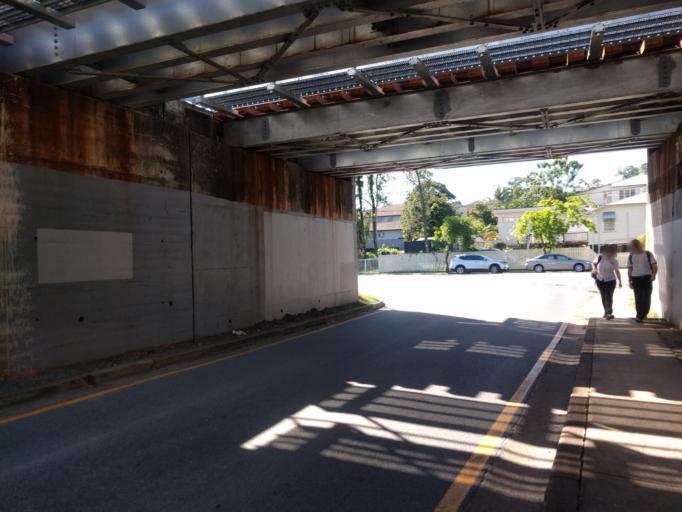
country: AU
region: Queensland
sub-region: Brisbane
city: Milton
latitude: -27.4749
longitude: 152.9979
